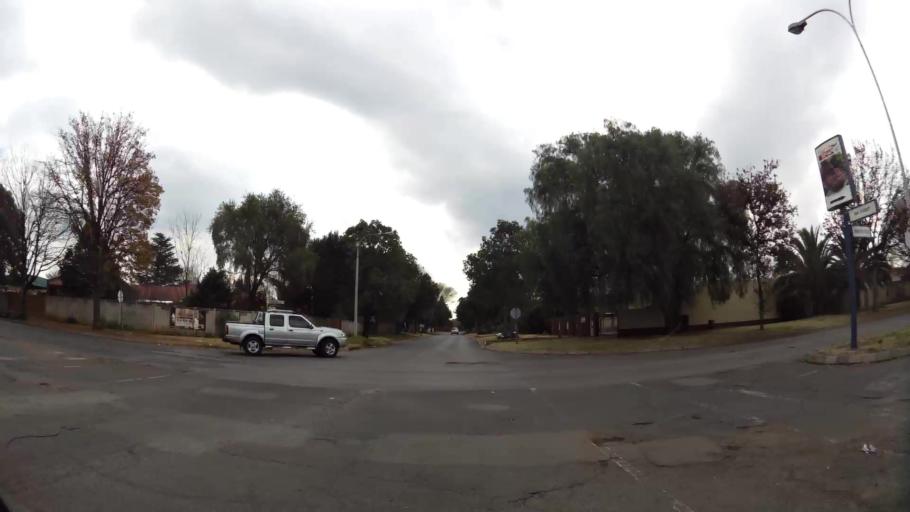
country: ZA
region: Gauteng
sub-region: Sedibeng District Municipality
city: Vanderbijlpark
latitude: -26.7327
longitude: 27.8458
